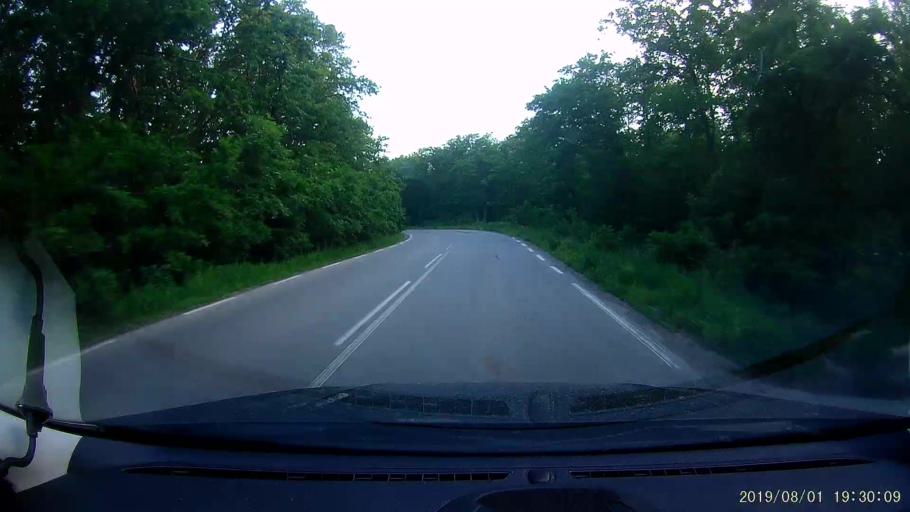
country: BG
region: Burgas
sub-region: Obshtina Sungurlare
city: Sungurlare
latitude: 42.8176
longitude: 26.8951
